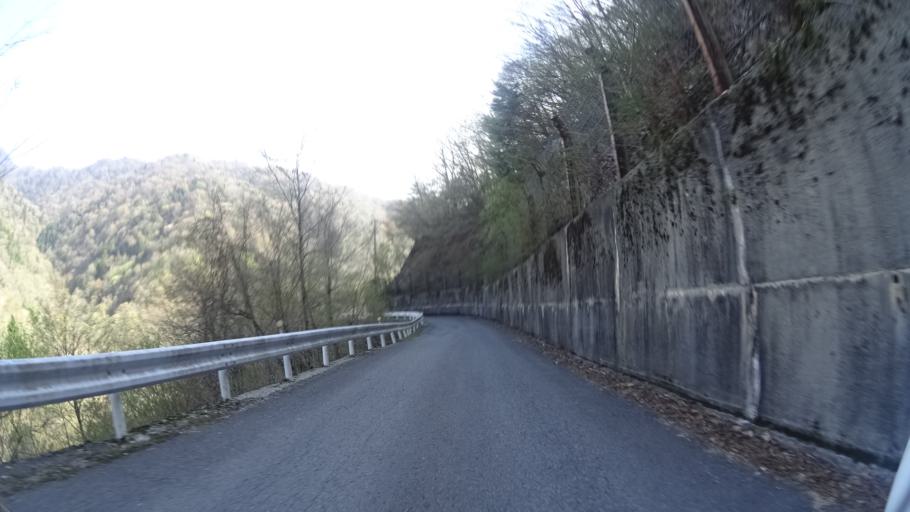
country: JP
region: Tokushima
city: Wakimachi
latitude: 33.8672
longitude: 134.0774
